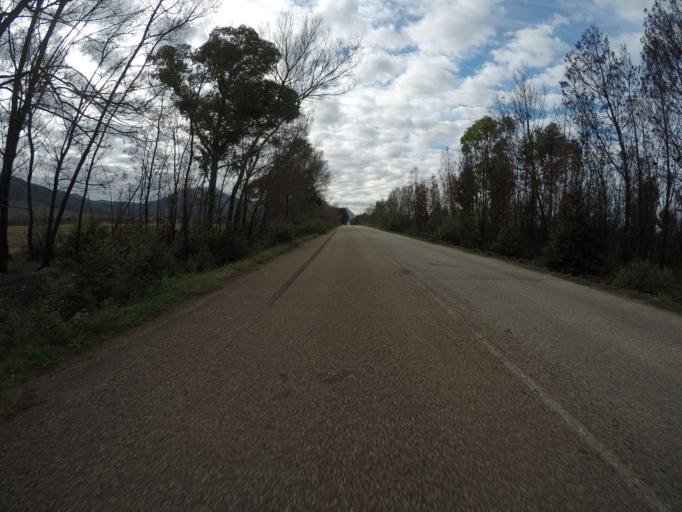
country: ZA
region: Eastern Cape
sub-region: Cacadu District Municipality
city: Kareedouw
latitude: -34.0149
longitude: 24.3216
